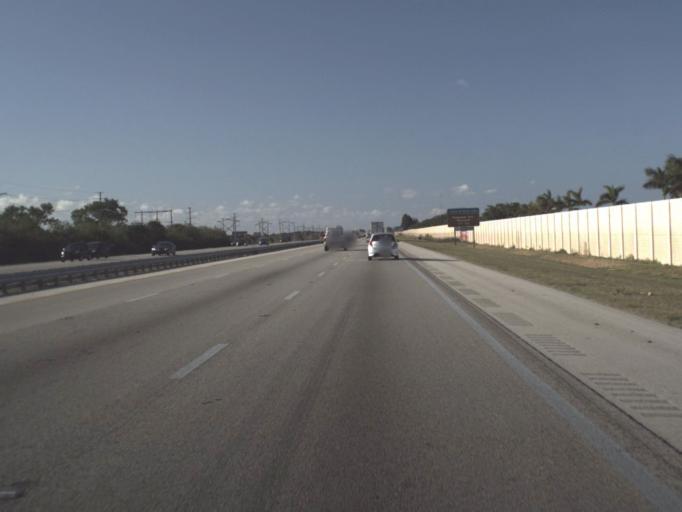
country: US
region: Florida
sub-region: Brevard County
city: June Park
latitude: 28.1033
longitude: -80.7058
